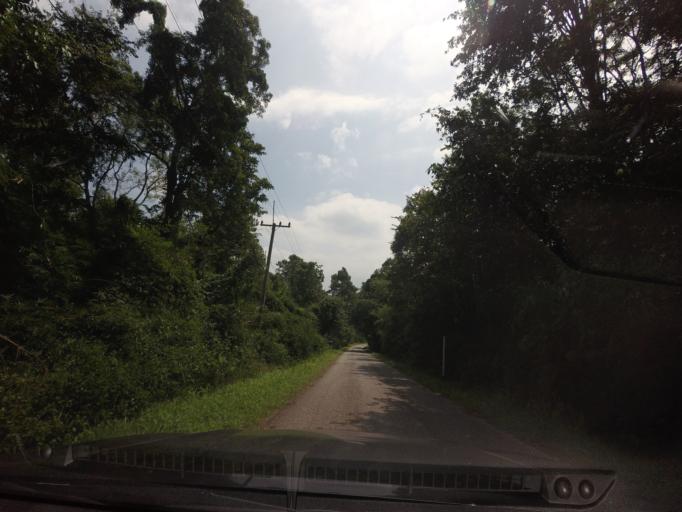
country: TH
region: Loei
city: Phu Ruea
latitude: 17.4688
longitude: 101.3552
